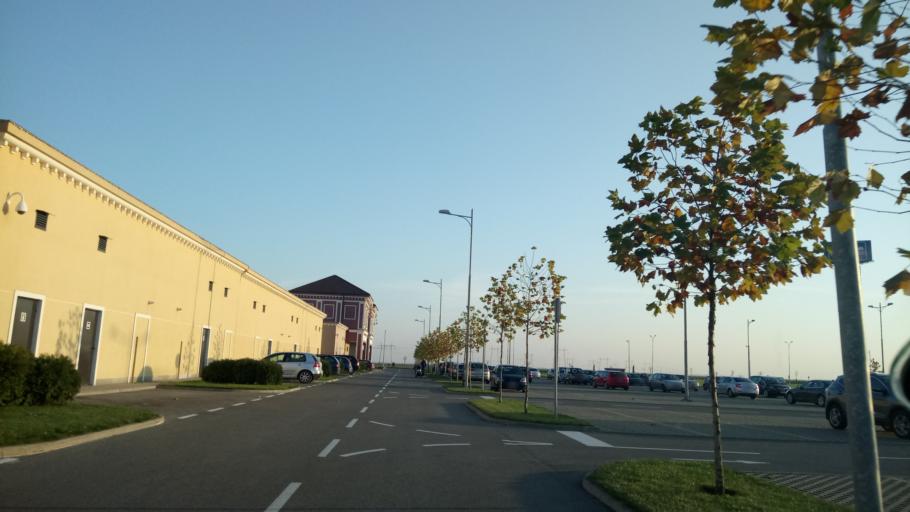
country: RS
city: Novi Karlovci
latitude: 45.0691
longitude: 20.1363
